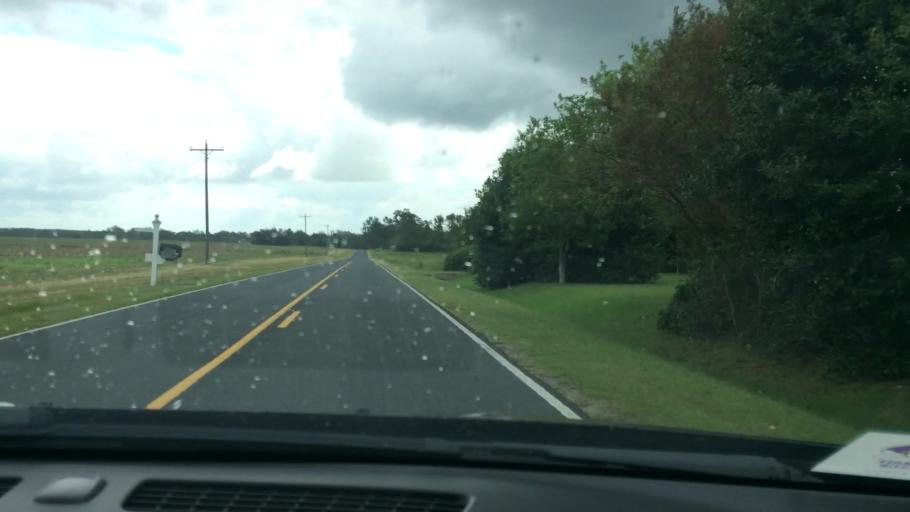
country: US
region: North Carolina
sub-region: Greene County
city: Maury
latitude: 35.5088
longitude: -77.5255
